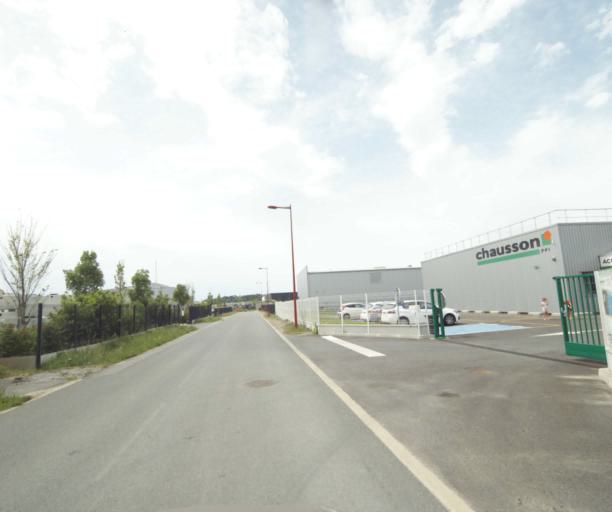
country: FR
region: Aquitaine
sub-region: Departement des Pyrenees-Atlantiques
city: Mouguerre
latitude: 43.4910
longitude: -1.4230
